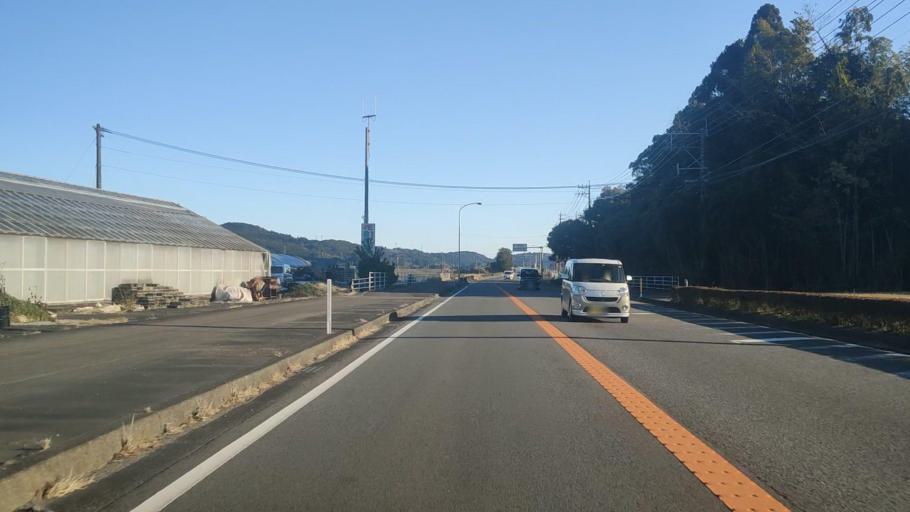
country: JP
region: Miyazaki
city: Takanabe
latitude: 32.3167
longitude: 131.5911
